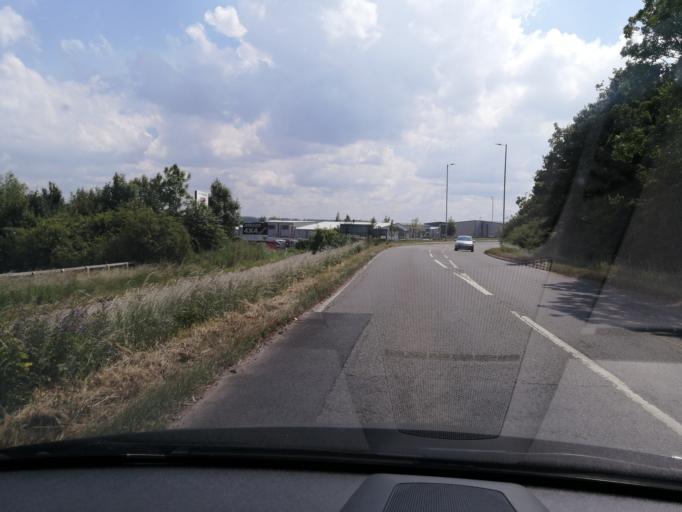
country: GB
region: England
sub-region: Cambridgeshire
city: Yaxley
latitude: 52.5282
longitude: -0.2382
